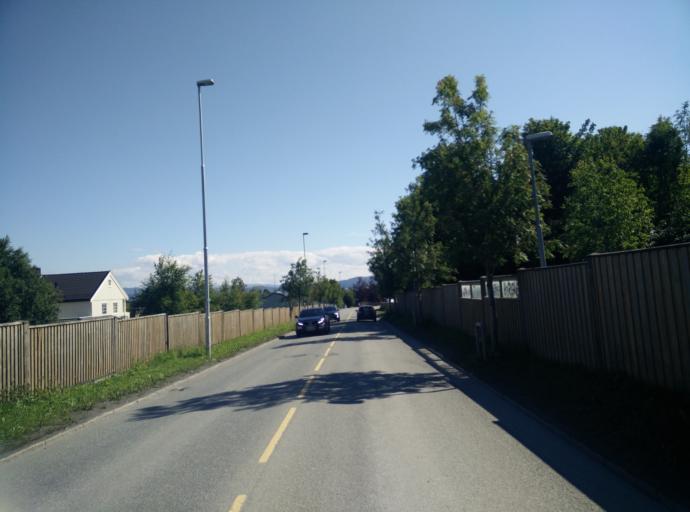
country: NO
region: Sor-Trondelag
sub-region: Trondheim
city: Trondheim
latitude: 63.4008
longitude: 10.3576
